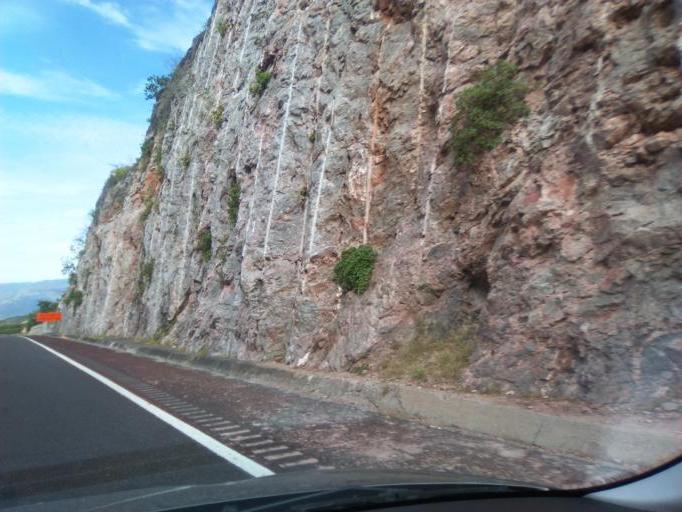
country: MX
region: Guerrero
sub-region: Huitzuco de los Figueroa
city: San Francisco Ozomatlan
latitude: 17.8715
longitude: -99.3994
